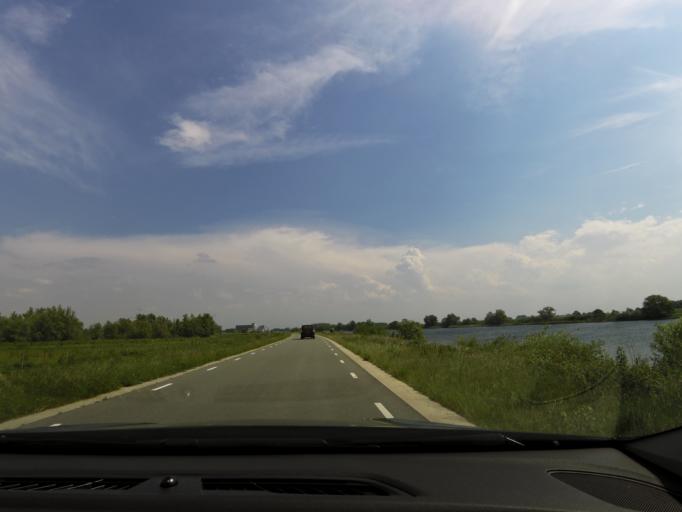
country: NL
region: North Brabant
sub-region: Gemeente Woudrichem
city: Woudrichem
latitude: 51.8055
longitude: 5.0261
